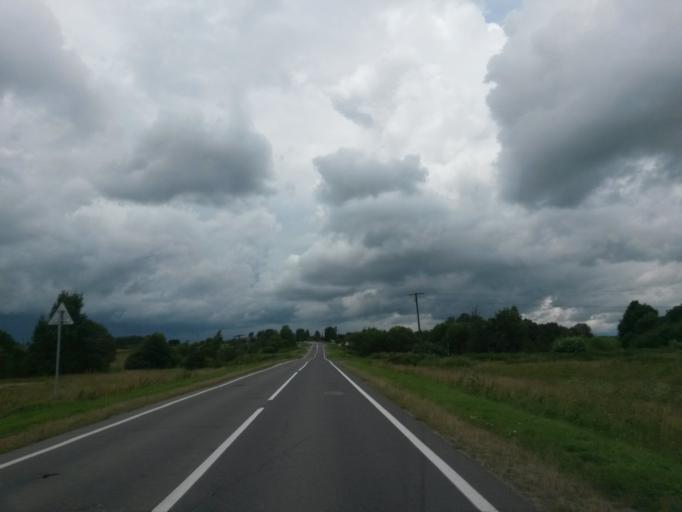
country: RU
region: Jaroslavl
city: Konstantinovskiy
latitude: 57.8408
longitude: 39.6519
